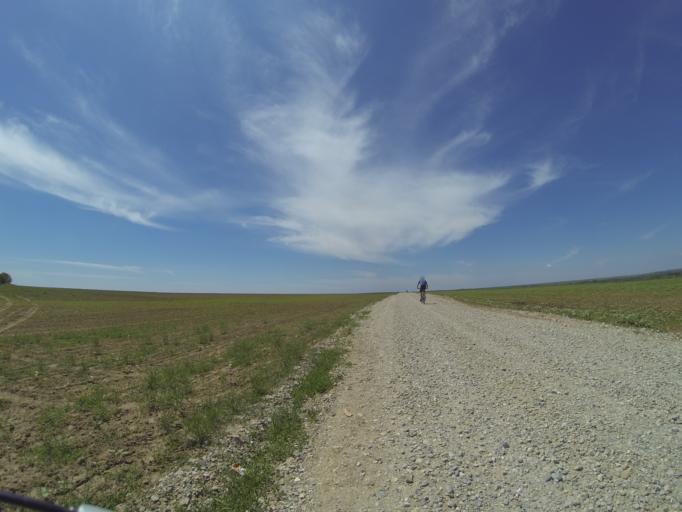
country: RO
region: Dolj
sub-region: Comuna Teslui
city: Teslui
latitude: 44.1891
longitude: 24.1680
